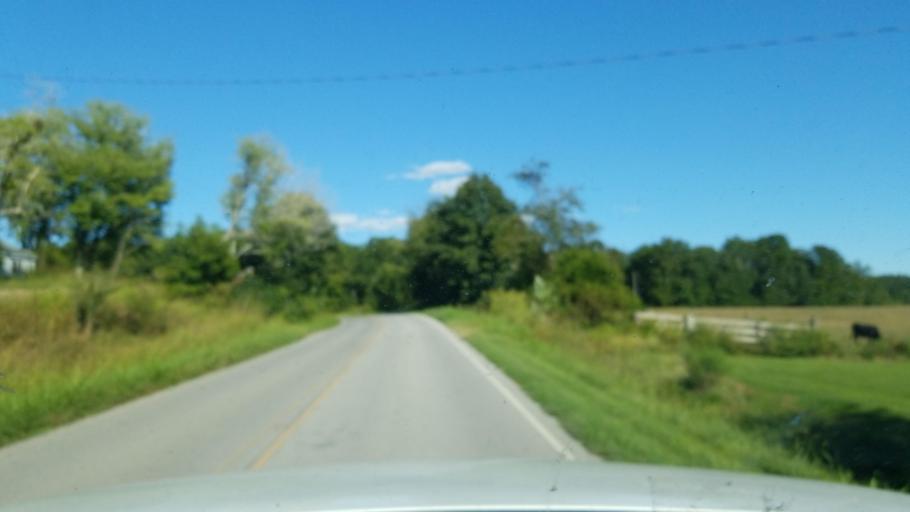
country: US
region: Illinois
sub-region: Hardin County
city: Elizabethtown
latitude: 37.5739
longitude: -88.3923
